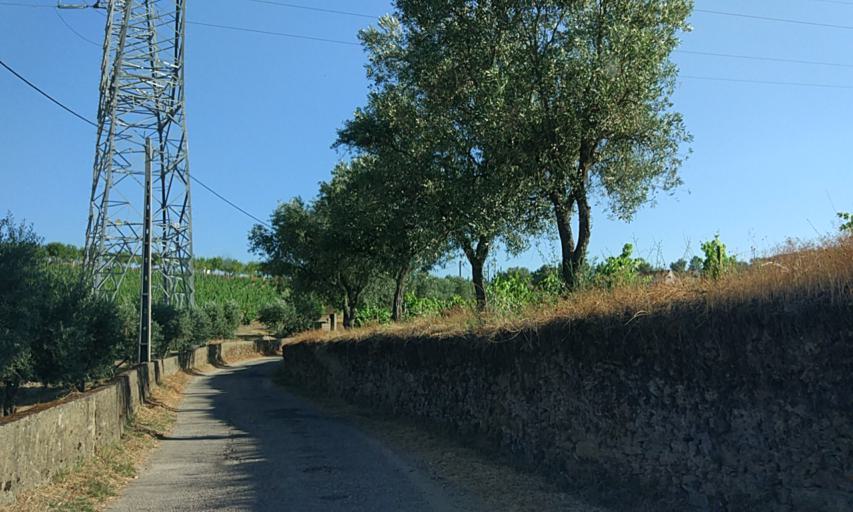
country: PT
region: Viseu
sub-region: Sao Joao da Pesqueira
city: Sao Joao da Pesqueira
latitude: 41.1566
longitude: -7.4199
